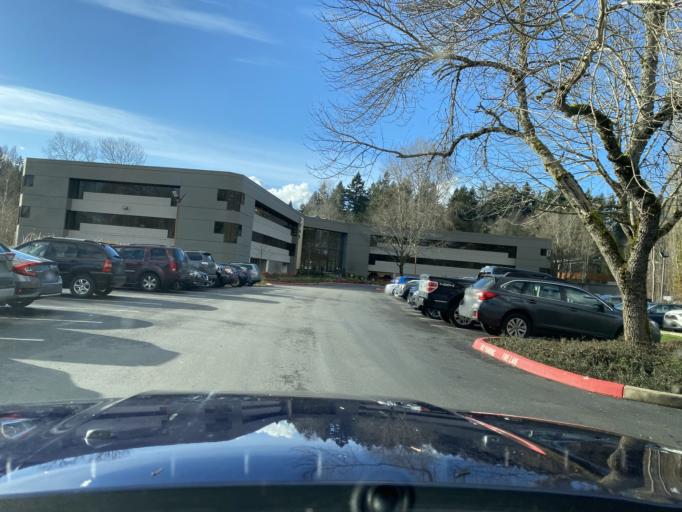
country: US
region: Washington
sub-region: King County
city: Bellevue
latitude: 47.5947
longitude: -122.1914
